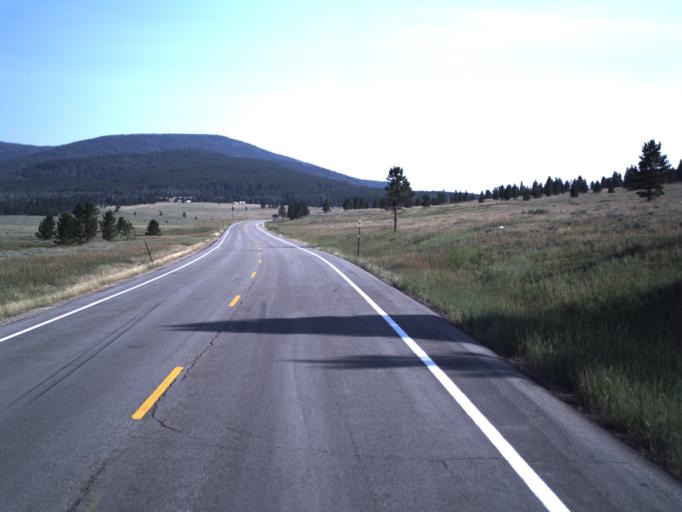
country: US
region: Utah
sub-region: Uintah County
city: Maeser
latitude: 40.7789
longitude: -109.4701
